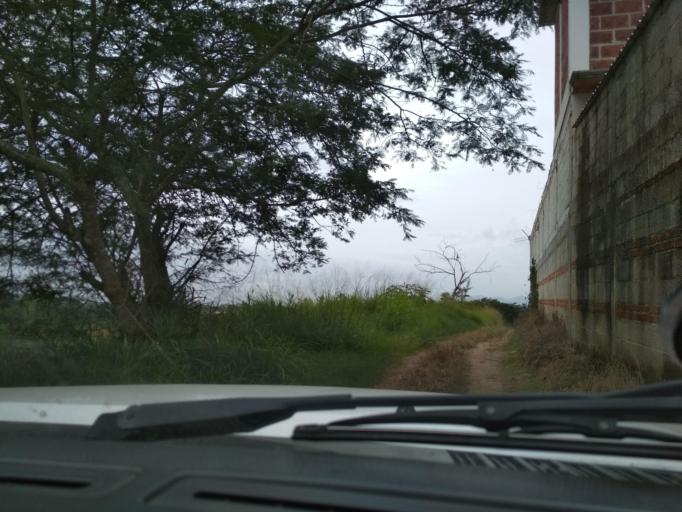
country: MX
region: Veracruz
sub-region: Emiliano Zapata
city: Dos Rios
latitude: 19.5316
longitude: -96.8098
